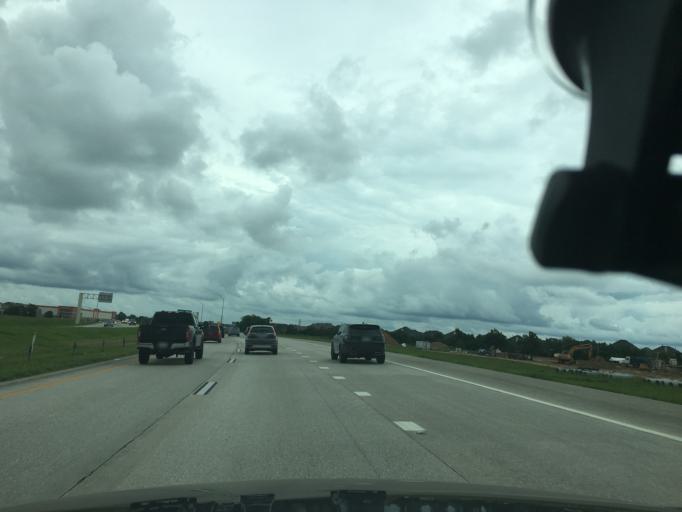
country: US
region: Texas
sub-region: Harris County
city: Tomball
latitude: 30.0794
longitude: -95.5399
